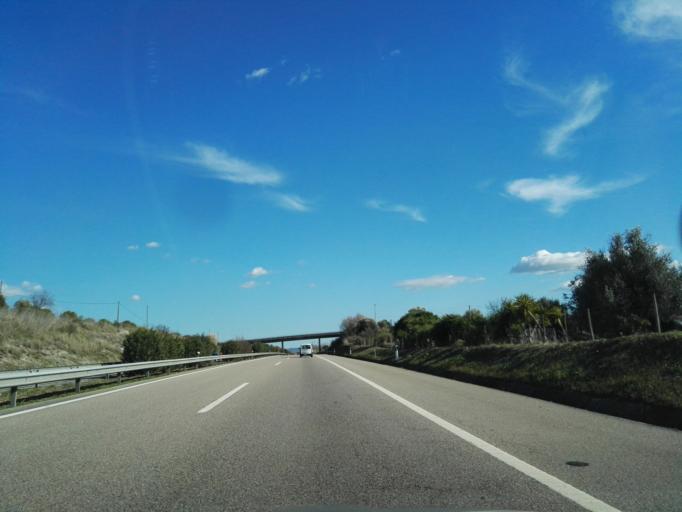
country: PT
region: Santarem
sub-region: Torres Novas
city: Torres Novas
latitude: 39.4686
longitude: -8.5665
